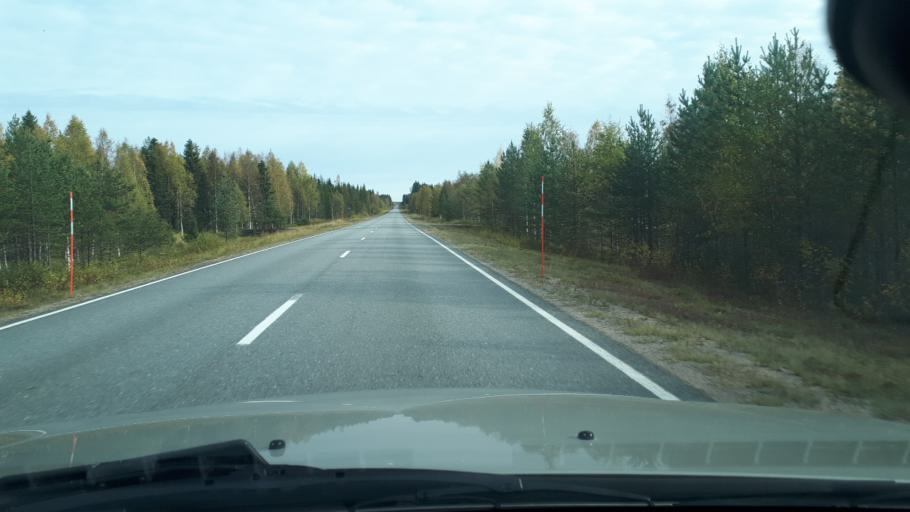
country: FI
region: Lapland
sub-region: Rovaniemi
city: Ranua
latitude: 65.9681
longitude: 26.0918
